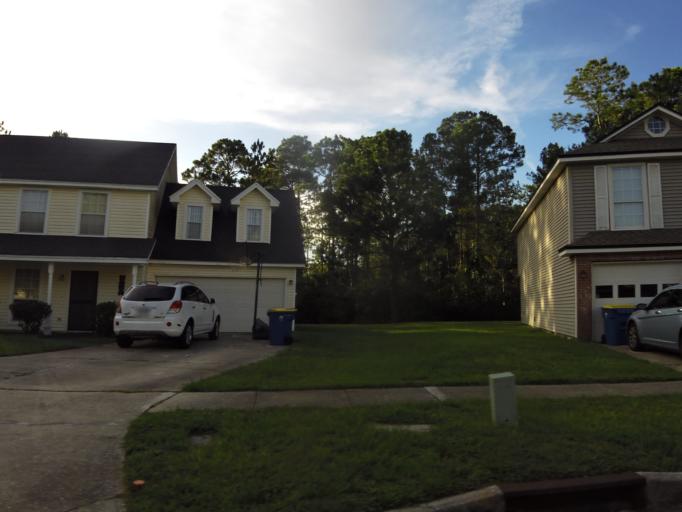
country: US
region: Florida
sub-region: Duval County
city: Jacksonville
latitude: 30.4458
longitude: -81.6841
